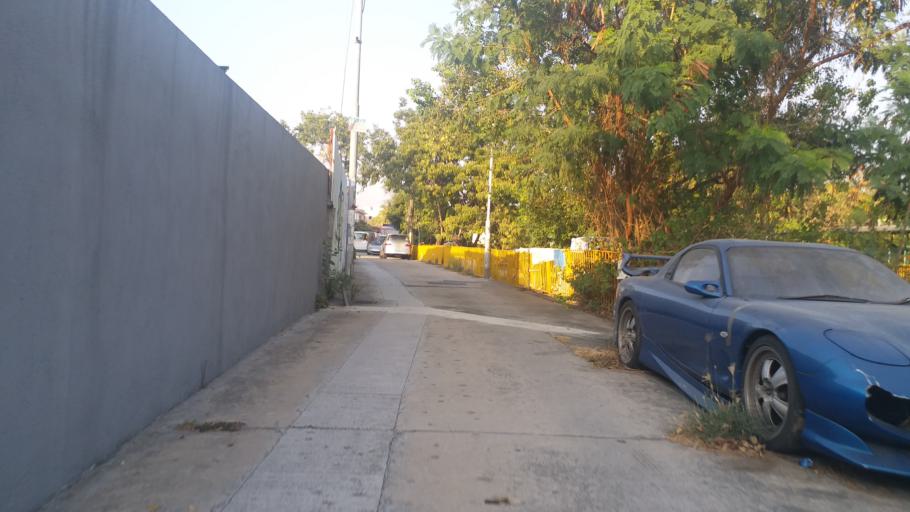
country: HK
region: Tuen Mun
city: Tuen Mun
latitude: 22.4198
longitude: 113.9811
